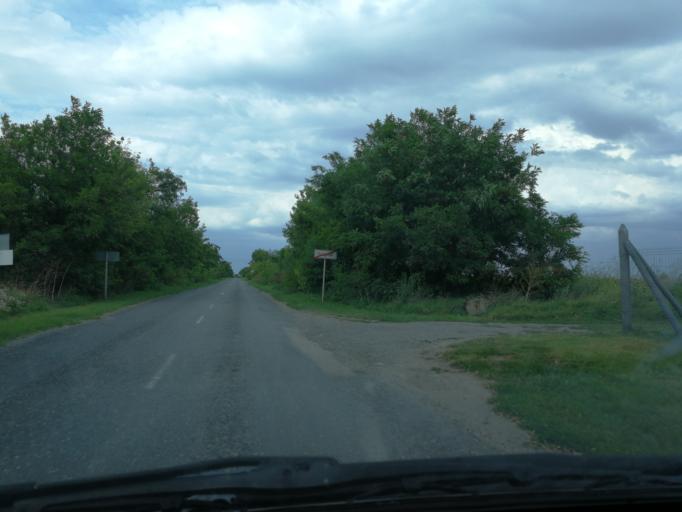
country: HU
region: Bacs-Kiskun
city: Kalocsa
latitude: 46.4715
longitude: 19.0441
